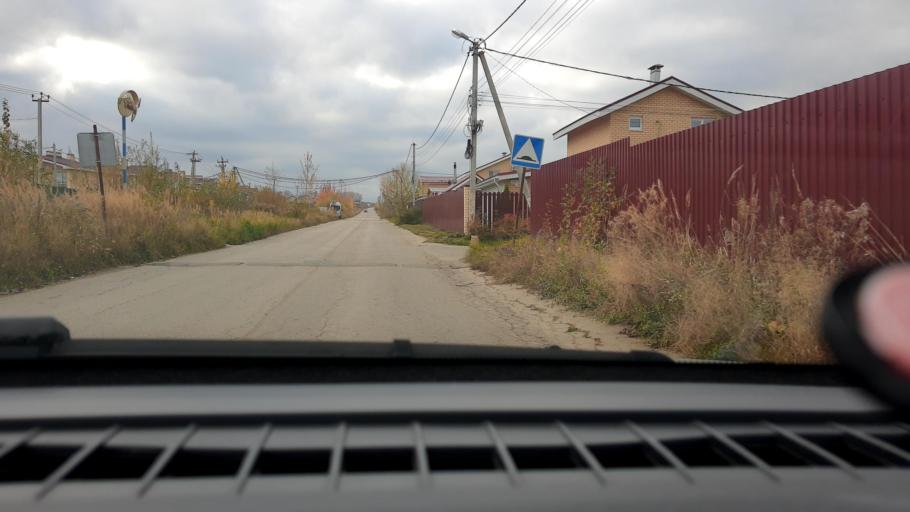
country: RU
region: Nizjnij Novgorod
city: Afonino
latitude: 56.1978
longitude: 44.0955
